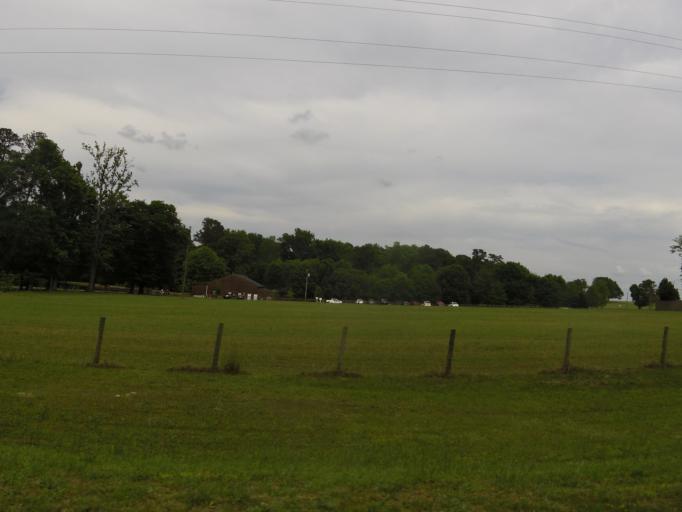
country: US
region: Georgia
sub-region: McDuffie County
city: Thomson
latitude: 33.4148
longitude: -82.4823
